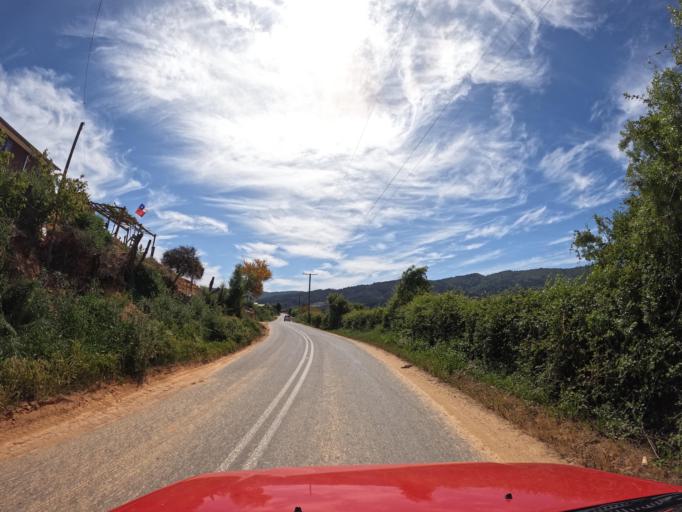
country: CL
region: Maule
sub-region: Provincia de Talca
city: Constitucion
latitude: -34.9936
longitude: -71.9938
